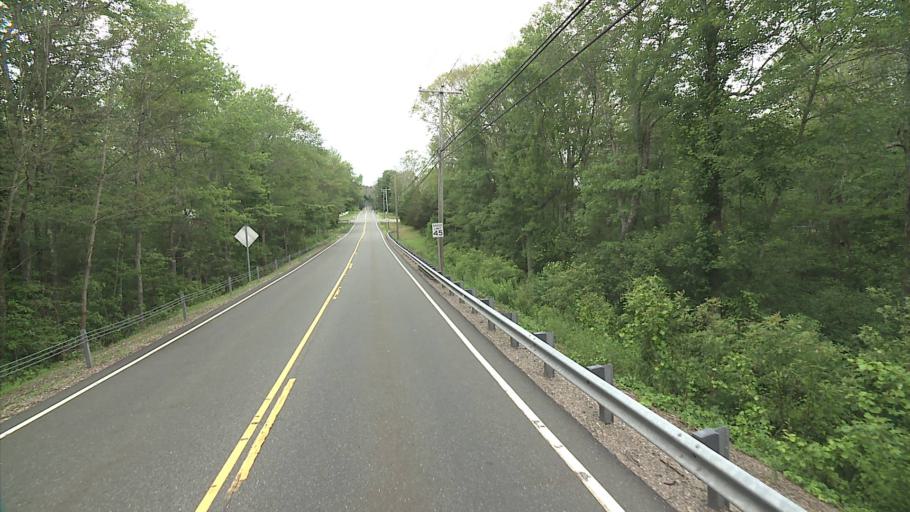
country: US
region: Connecticut
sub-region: New London County
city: Ledyard Center
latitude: 41.4588
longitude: -72.0156
